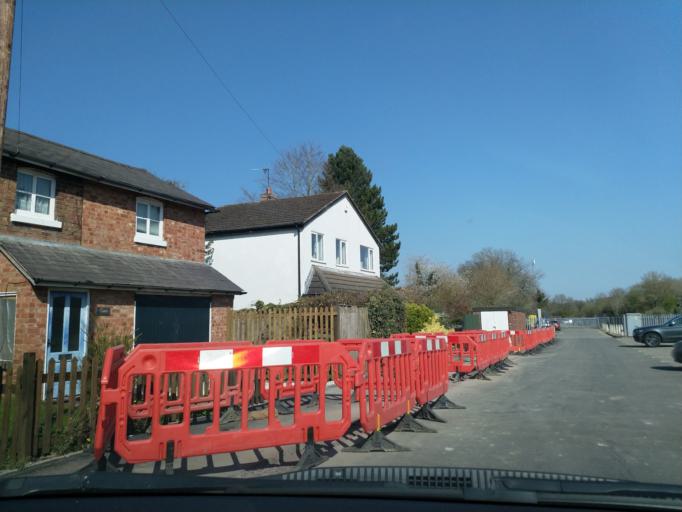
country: GB
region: England
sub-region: Warwickshire
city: Wroxall
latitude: 52.2954
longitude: -1.6730
